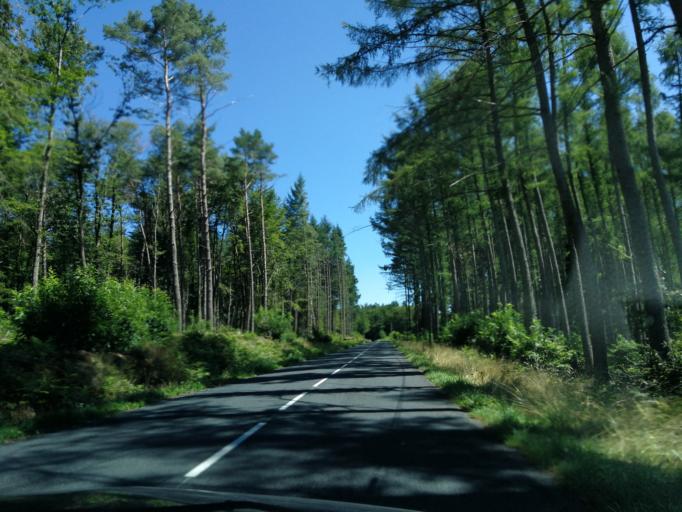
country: FR
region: Limousin
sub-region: Departement de la Correze
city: Argentat
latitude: 45.0031
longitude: 2.0456
